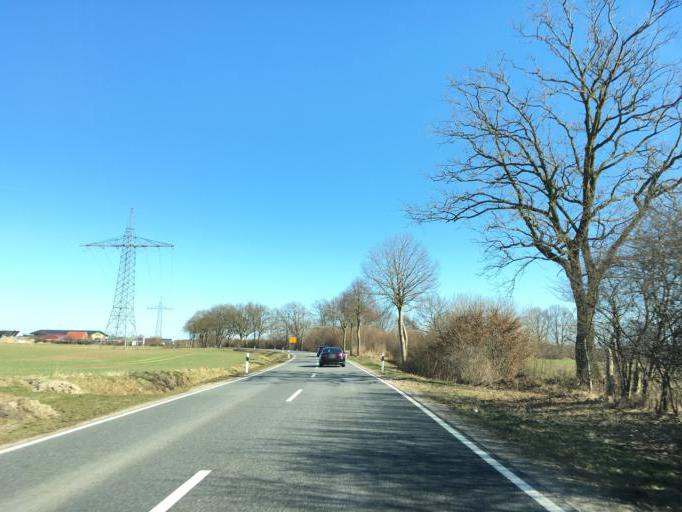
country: DE
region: Schleswig-Holstein
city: Goldenitz
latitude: 53.7289
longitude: 10.6252
